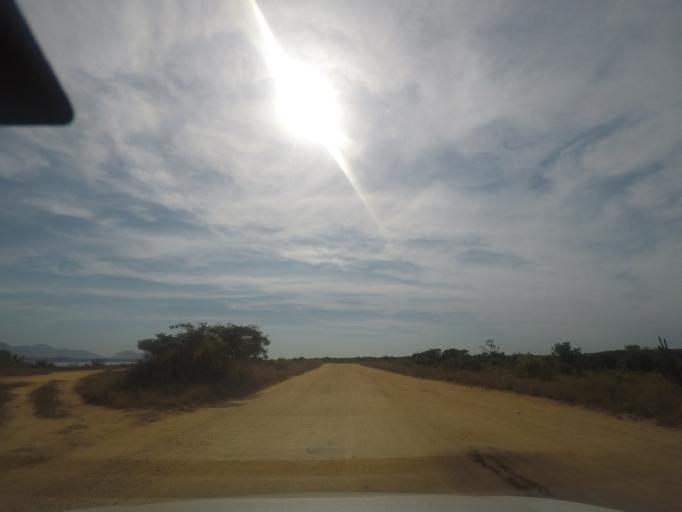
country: BR
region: Rio de Janeiro
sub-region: Marica
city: Marica
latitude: -22.9588
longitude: -42.8778
